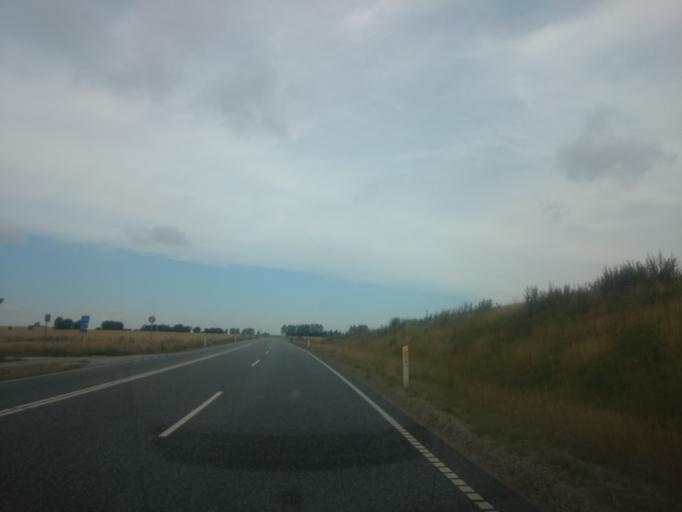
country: DK
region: South Denmark
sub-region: Vejle Kommune
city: Jelling
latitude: 55.6920
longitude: 9.3793
